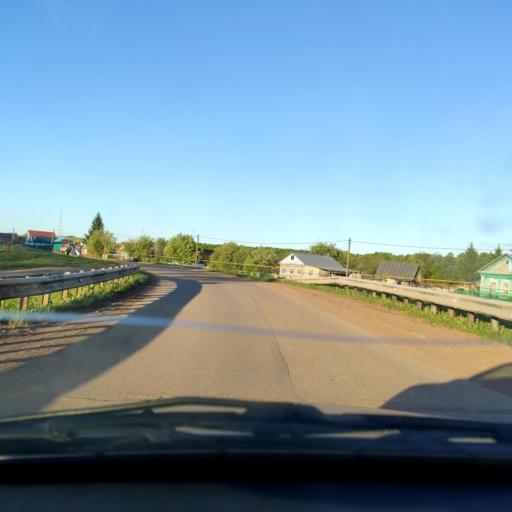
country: RU
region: Bashkortostan
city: Yazykovo
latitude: 55.0253
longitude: 56.2150
